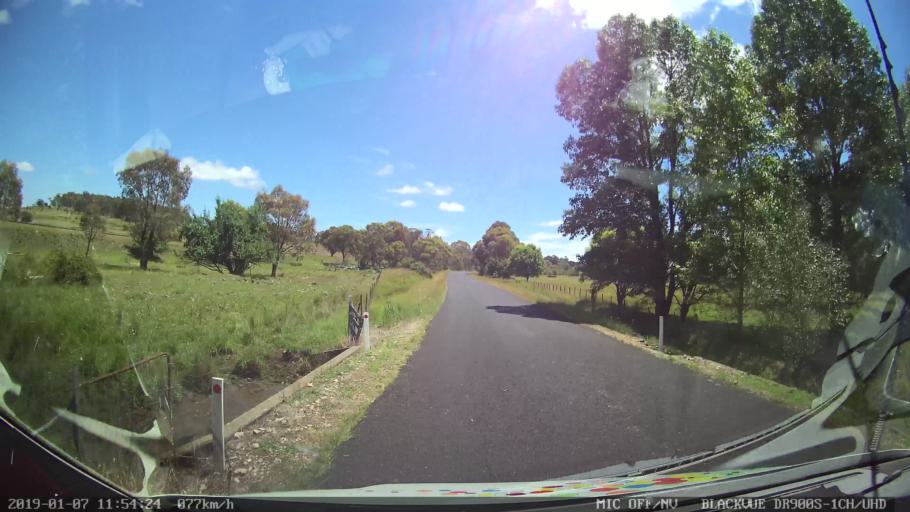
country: AU
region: New South Wales
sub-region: Guyra
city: Guyra
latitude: -30.2966
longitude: 151.6643
